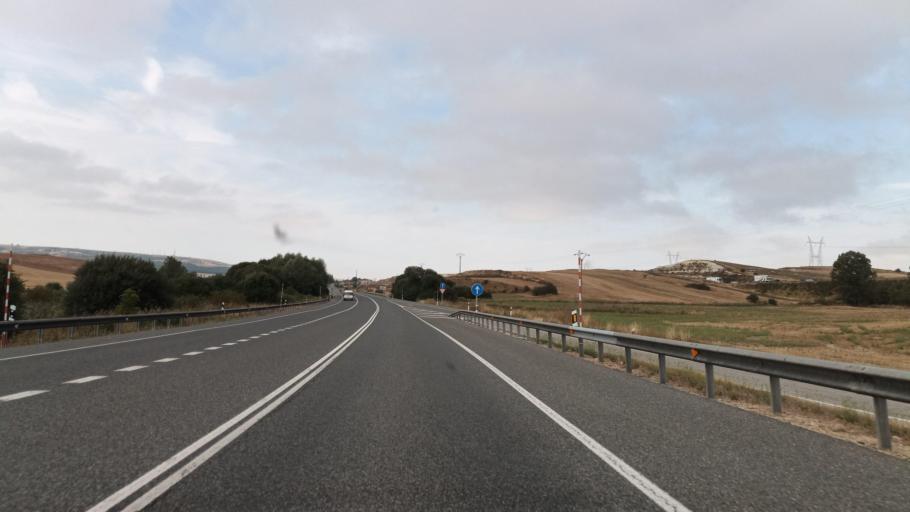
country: ES
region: Castille and Leon
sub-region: Provincia de Burgos
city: Quintanapalla
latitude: 42.4225
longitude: -3.5131
